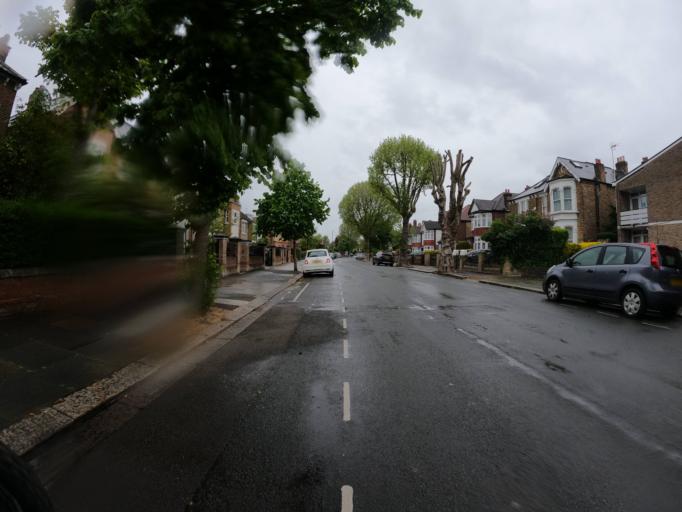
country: GB
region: England
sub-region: Greater London
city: Acton
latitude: 51.5126
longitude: -0.2757
